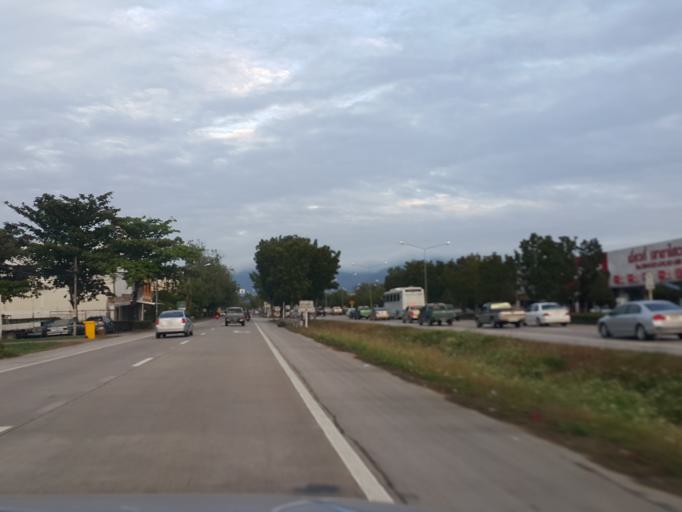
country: TH
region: Lampang
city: Lampang
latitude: 18.2821
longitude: 99.5032
